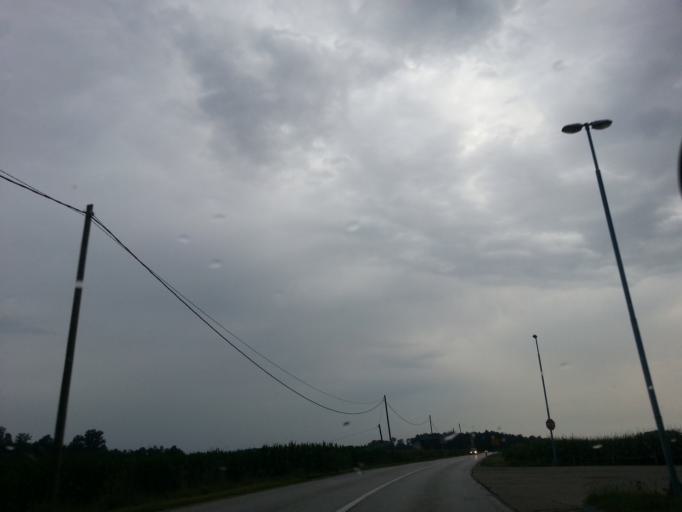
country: HR
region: Vukovarsko-Srijemska
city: Soljani
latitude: 44.8300
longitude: 19.0173
